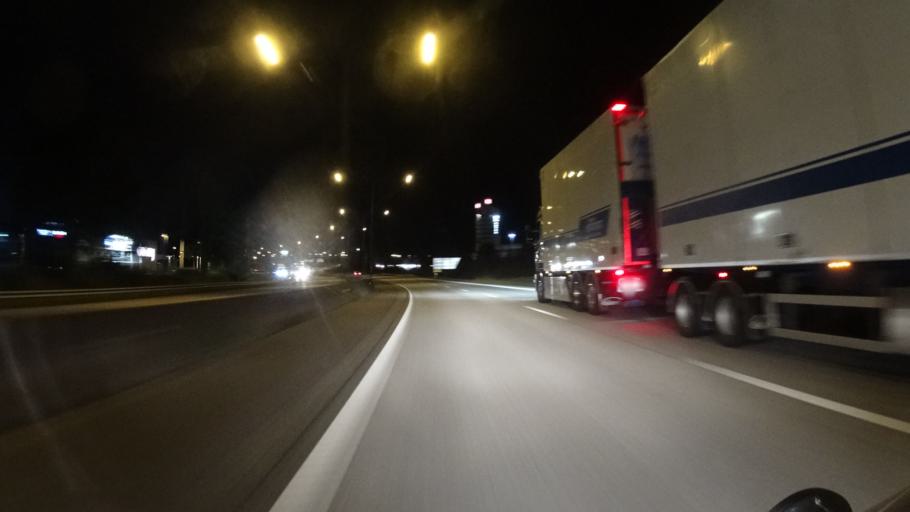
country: SE
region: Joenkoeping
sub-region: Jonkopings Kommun
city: Jonkoping
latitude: 57.7601
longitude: 14.1838
